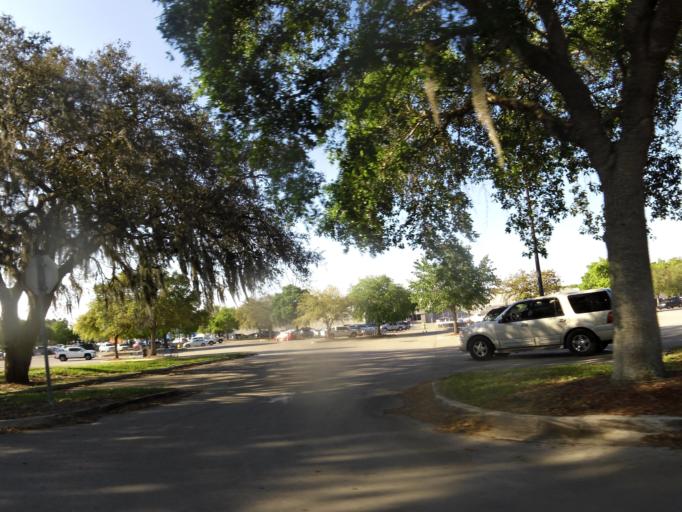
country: US
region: Florida
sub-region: Putnam County
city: Palatka
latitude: 29.6367
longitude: -81.6807
